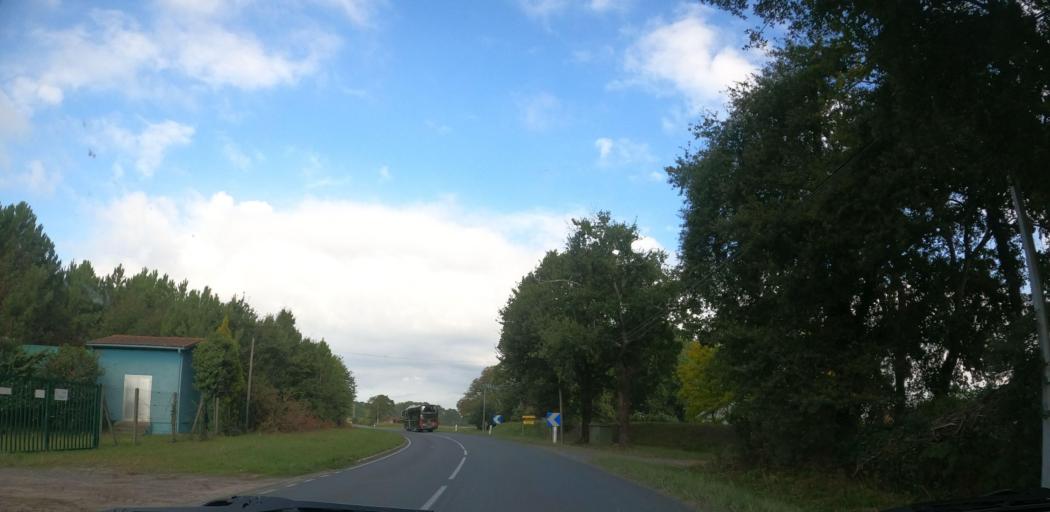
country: FR
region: Aquitaine
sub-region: Departement des Landes
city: Soustons
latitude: 43.7429
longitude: -1.3000
